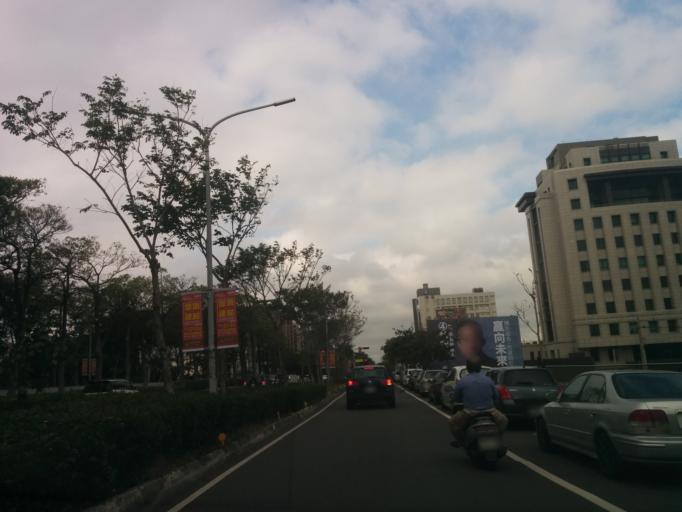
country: TW
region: Taiwan
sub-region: Hsinchu
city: Hsinchu
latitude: 24.8013
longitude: 121.0018
